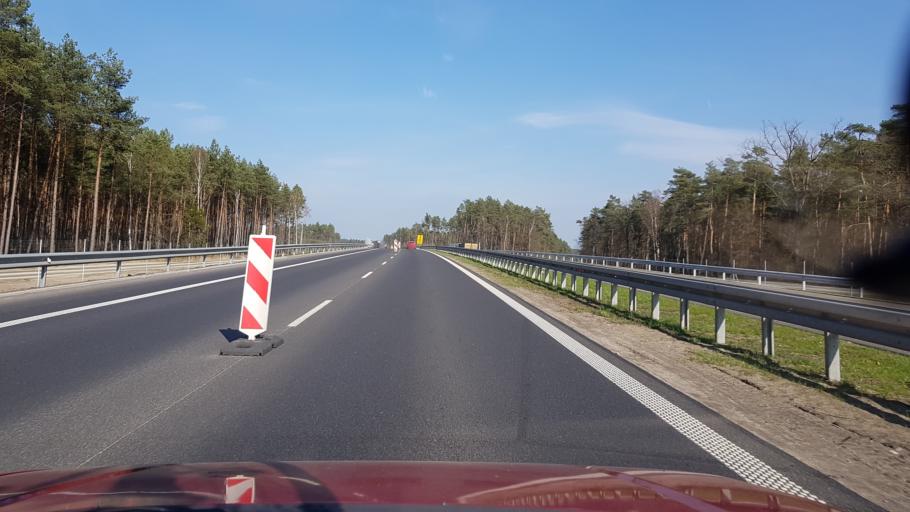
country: PL
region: West Pomeranian Voivodeship
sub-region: Powiat goleniowski
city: Goleniow
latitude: 53.6031
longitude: 14.8904
